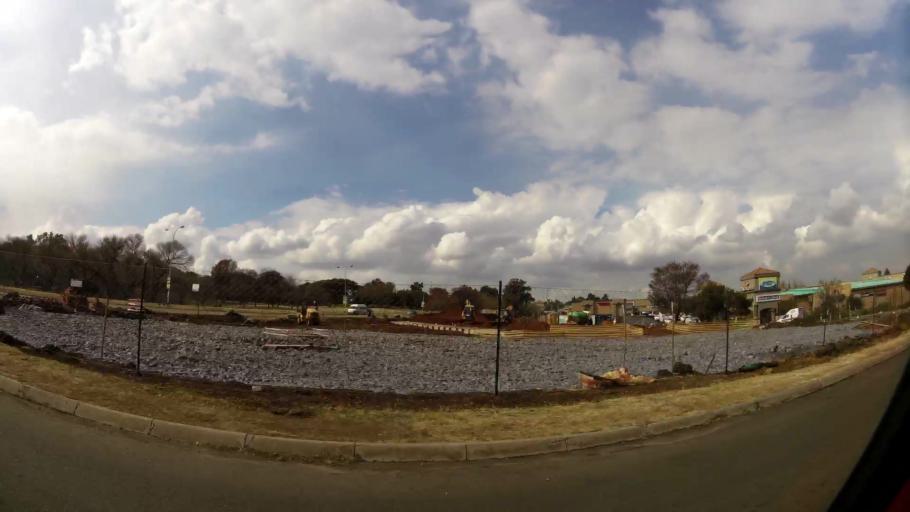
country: ZA
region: Gauteng
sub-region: Sedibeng District Municipality
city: Vanderbijlpark
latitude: -26.7331
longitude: 27.8376
